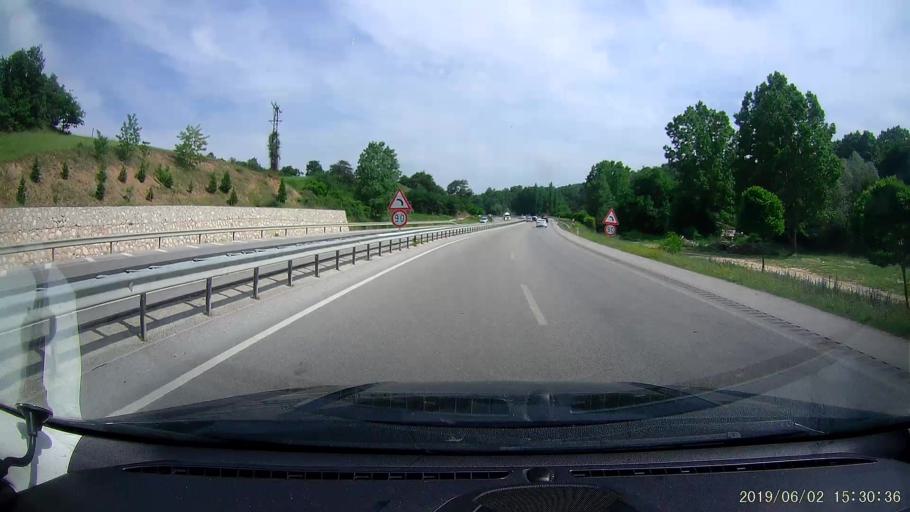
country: TR
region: Amasya
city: Saraycik
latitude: 40.9527
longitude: 35.1129
